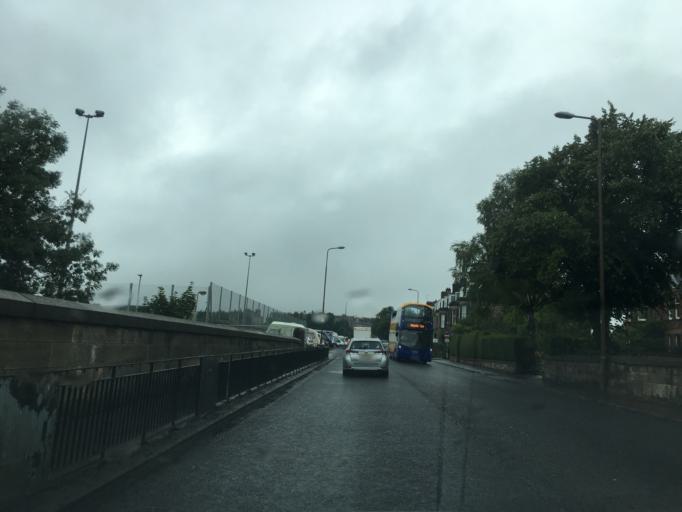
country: GB
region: Scotland
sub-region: Edinburgh
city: Edinburgh
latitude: 55.9721
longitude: -3.2011
